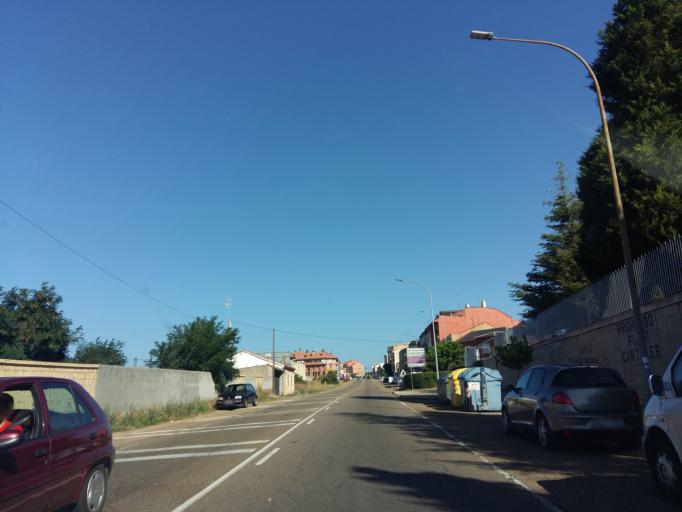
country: ES
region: Castille and Leon
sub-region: Provincia de Leon
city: Astorga
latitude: 42.4564
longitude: -6.0613
